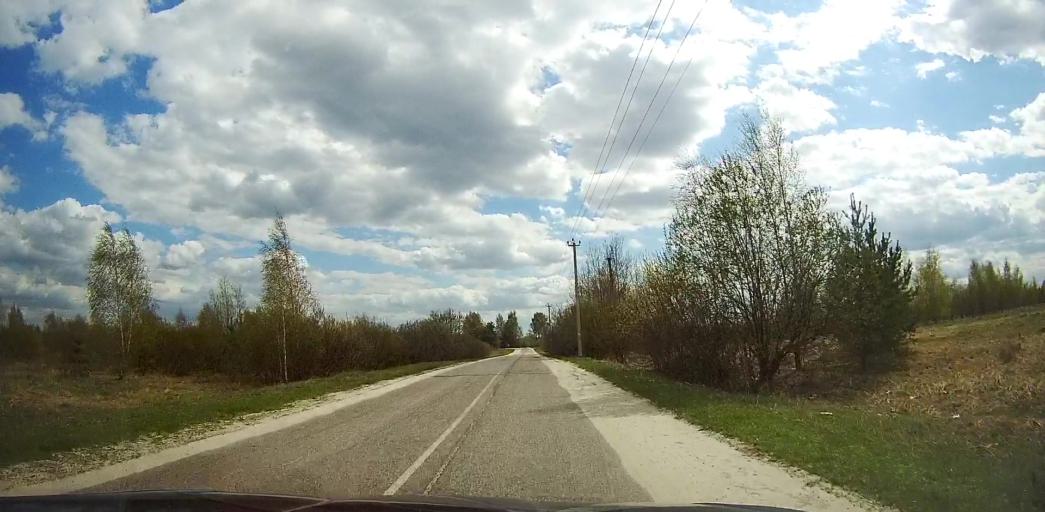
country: RU
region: Moskovskaya
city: Davydovo
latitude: 55.6346
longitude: 38.7828
